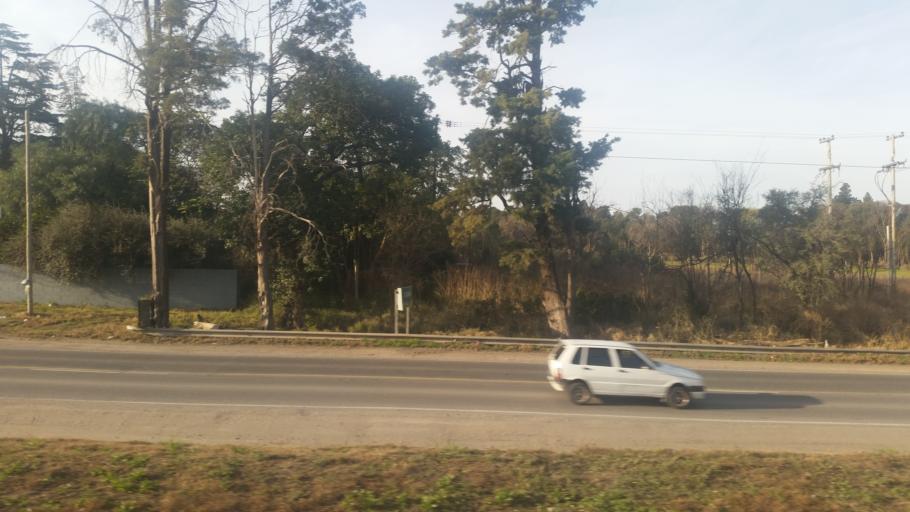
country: AR
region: Cordoba
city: Toledo
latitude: -31.4913
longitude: -64.0761
